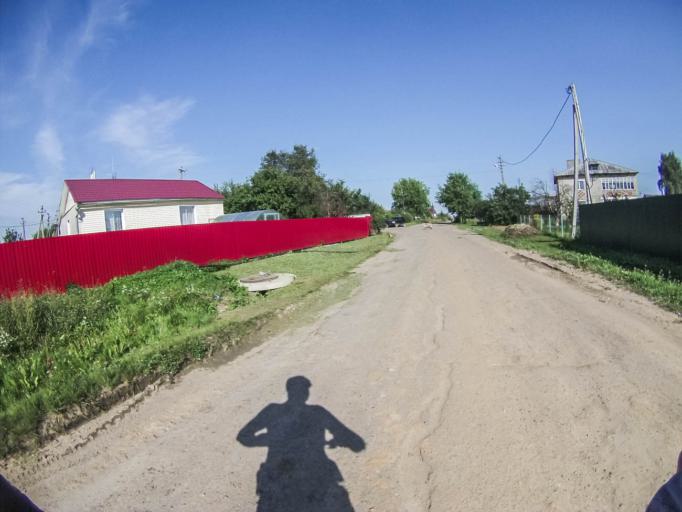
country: RU
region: Jaroslavl
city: Myshkin
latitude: 57.7827
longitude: 38.4373
